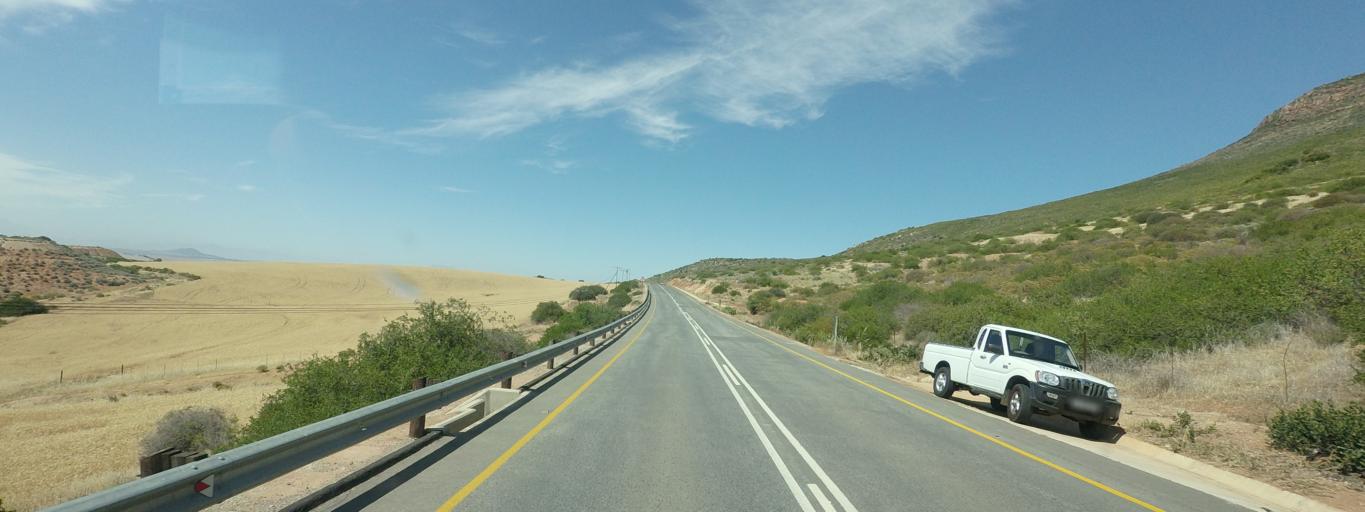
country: ZA
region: Western Cape
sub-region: West Coast District Municipality
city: Piketberg
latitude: -32.9250
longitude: 18.7562
